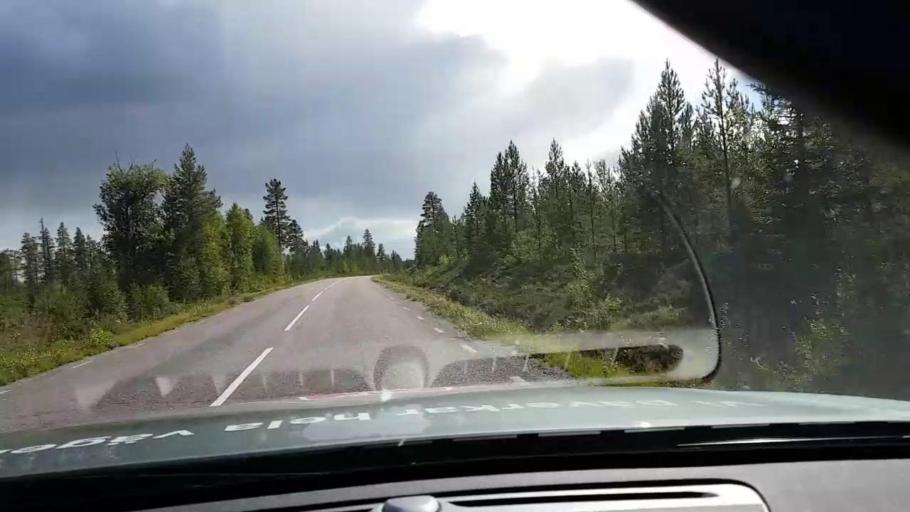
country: SE
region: Vaesterbotten
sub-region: Asele Kommun
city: Asele
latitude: 63.8930
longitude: 17.3499
